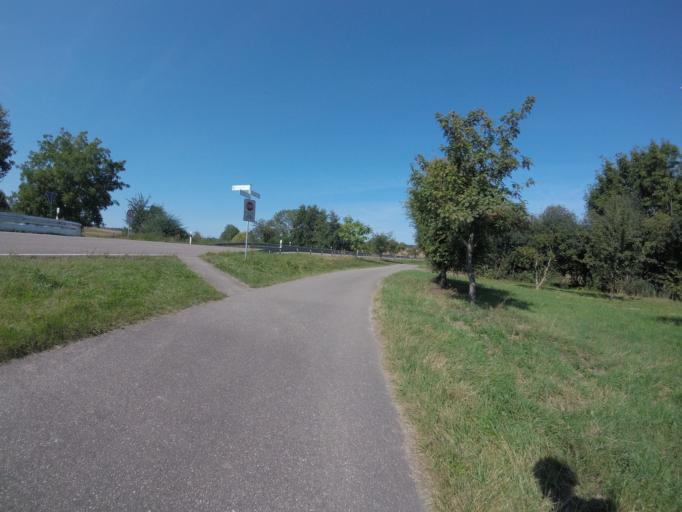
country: DE
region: Baden-Wuerttemberg
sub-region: Regierungsbezirk Stuttgart
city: Grossbottwar
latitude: 49.0126
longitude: 9.2721
